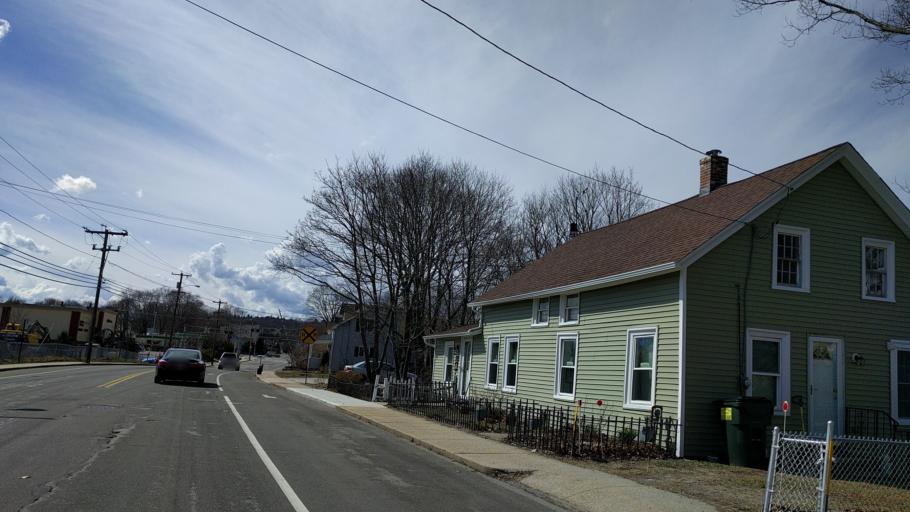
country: US
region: Massachusetts
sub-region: Worcester County
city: Uxbridge
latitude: 42.0918
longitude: -71.6403
